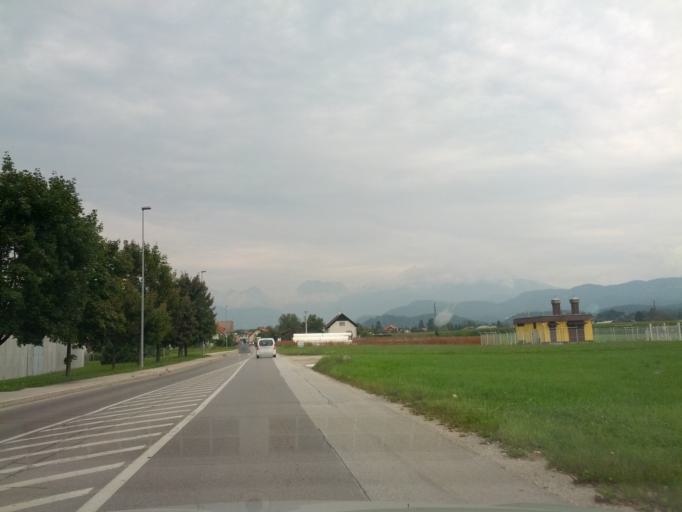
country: SI
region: Domzale
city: Radomlje
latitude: 46.1638
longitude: 14.6087
